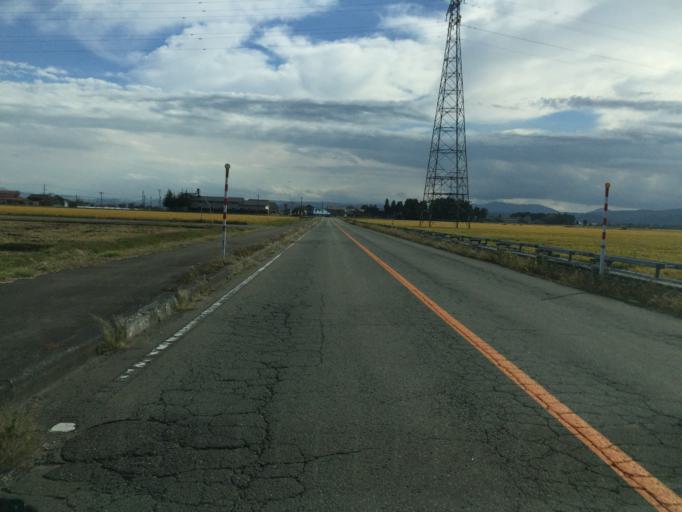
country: JP
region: Fukushima
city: Inawashiro
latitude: 37.5478
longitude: 140.0782
